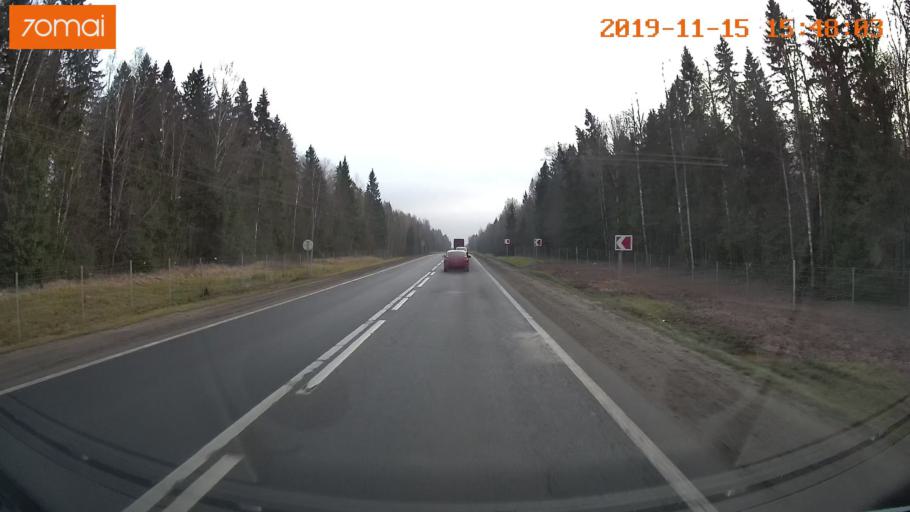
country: RU
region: Jaroslavl
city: Danilov
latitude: 57.9317
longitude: 40.0065
